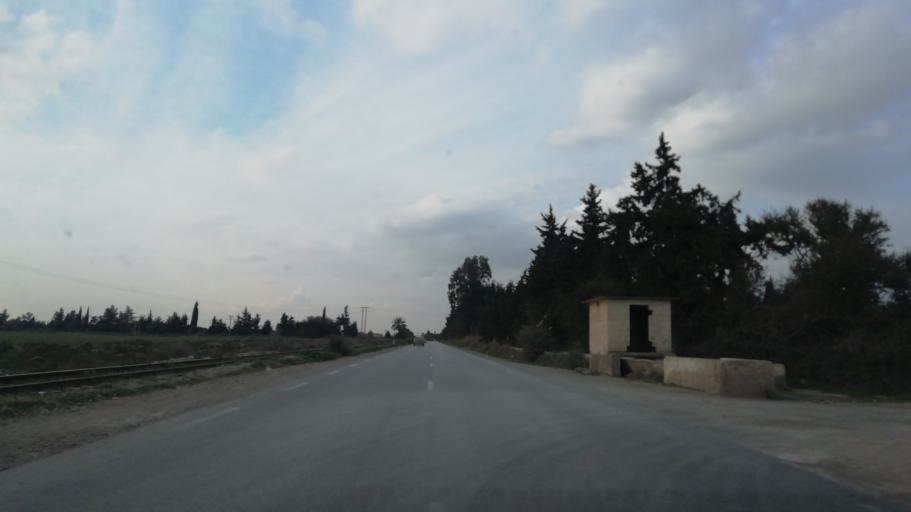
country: DZ
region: Mascara
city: Sig
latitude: 35.6633
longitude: 0.0048
